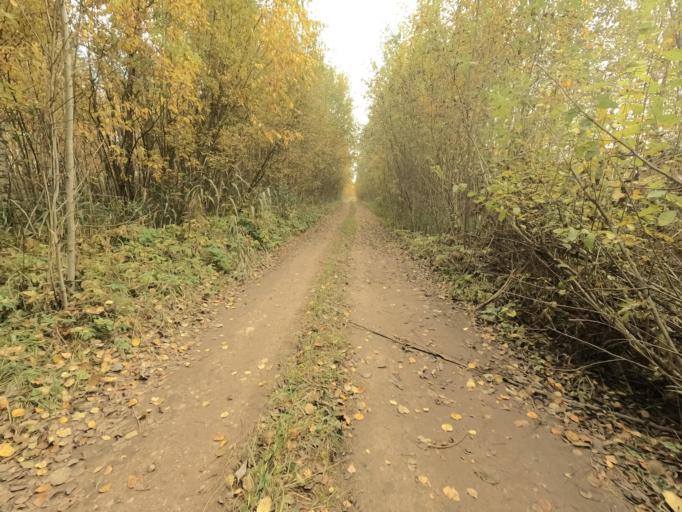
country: RU
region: Novgorod
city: Pankovka
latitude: 58.8756
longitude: 30.8745
